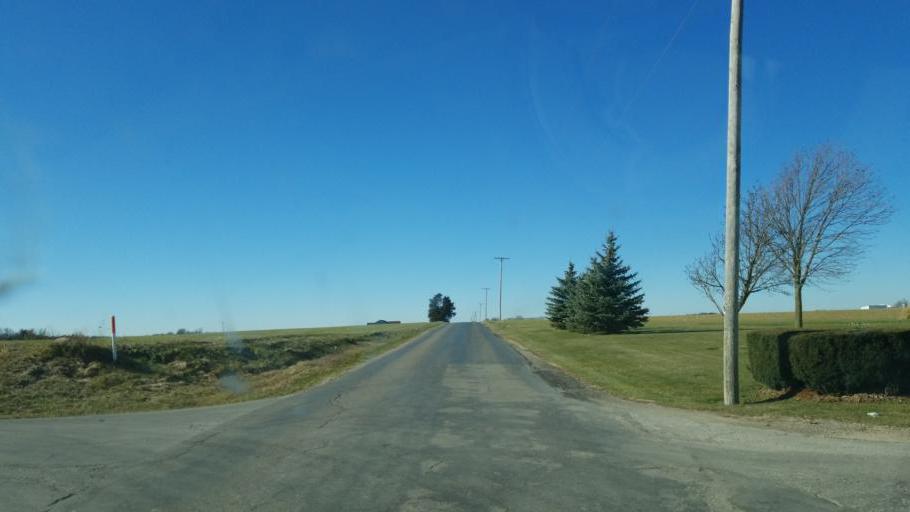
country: US
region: Ohio
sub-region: Huron County
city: Greenwich
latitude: 40.9608
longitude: -82.5218
